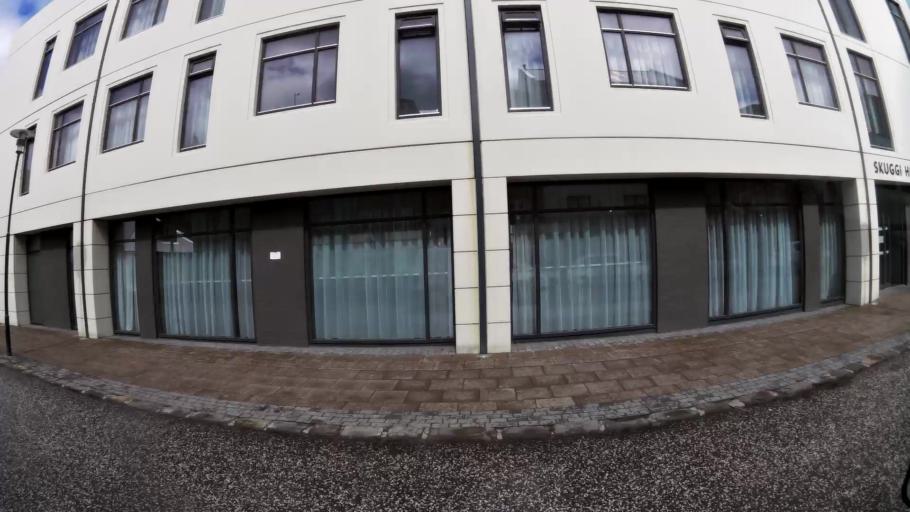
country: IS
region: Capital Region
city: Reykjavik
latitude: 64.1442
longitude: -21.9171
